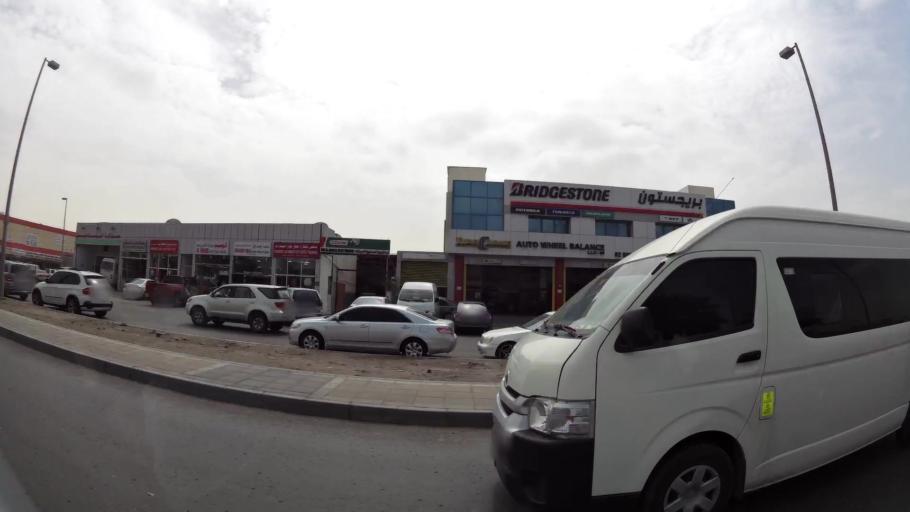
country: AE
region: Abu Dhabi
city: Abu Dhabi
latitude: 24.3733
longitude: 54.5147
